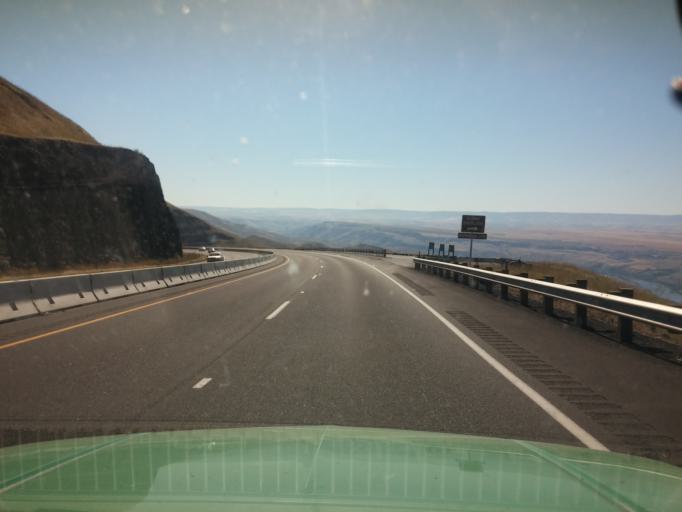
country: US
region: Idaho
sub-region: Nez Perce County
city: Lewiston
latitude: 46.4620
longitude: -116.9938
